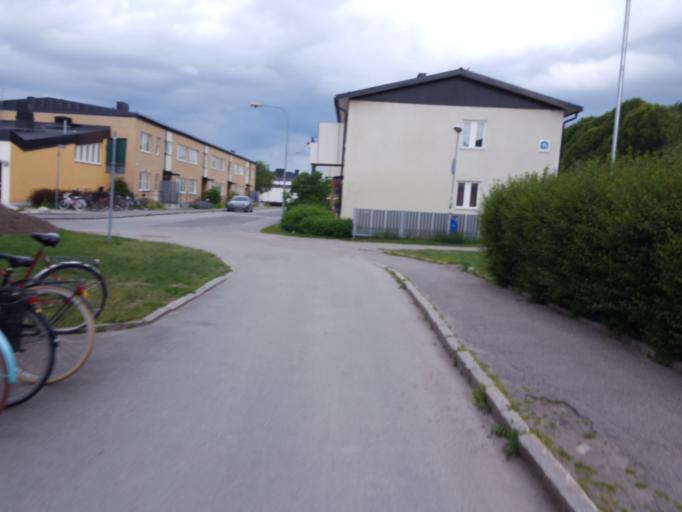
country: SE
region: Uppsala
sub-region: Uppsala Kommun
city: Uppsala
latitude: 59.8683
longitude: 17.6541
